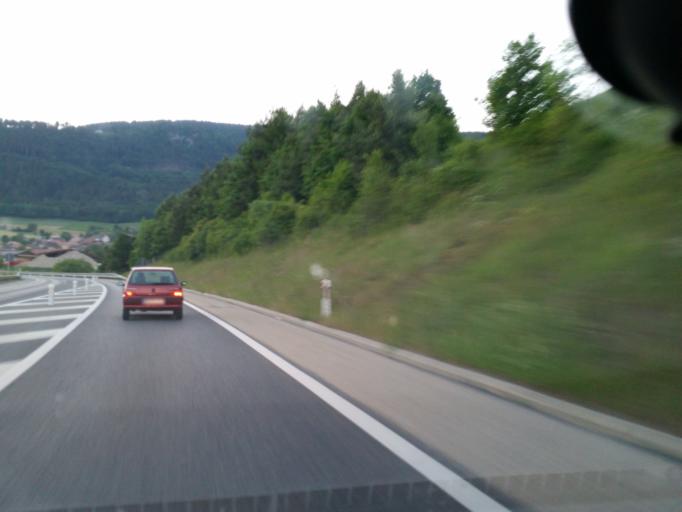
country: CH
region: Vaud
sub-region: Jura-Nord vaudois District
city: Orbe
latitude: 46.7359
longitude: 6.4662
